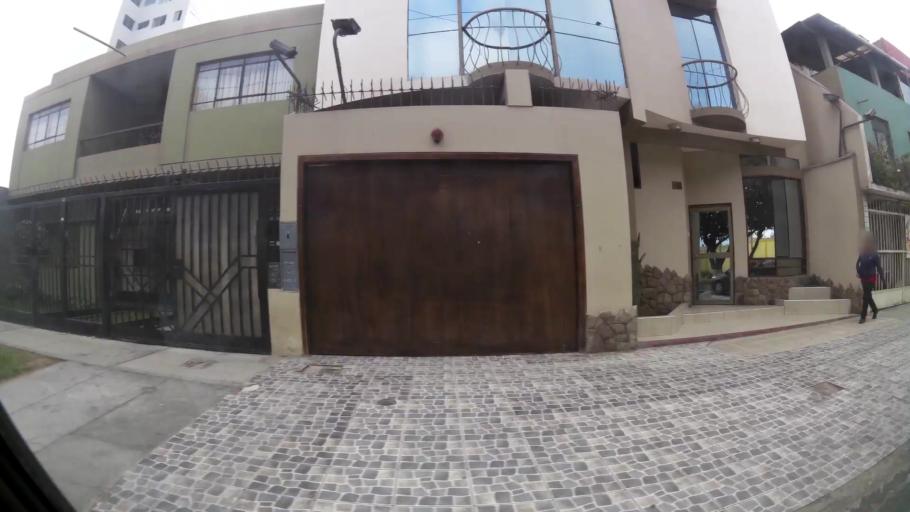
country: PE
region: La Libertad
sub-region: Provincia de Trujillo
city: Trujillo
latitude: -8.1023
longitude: -79.0279
